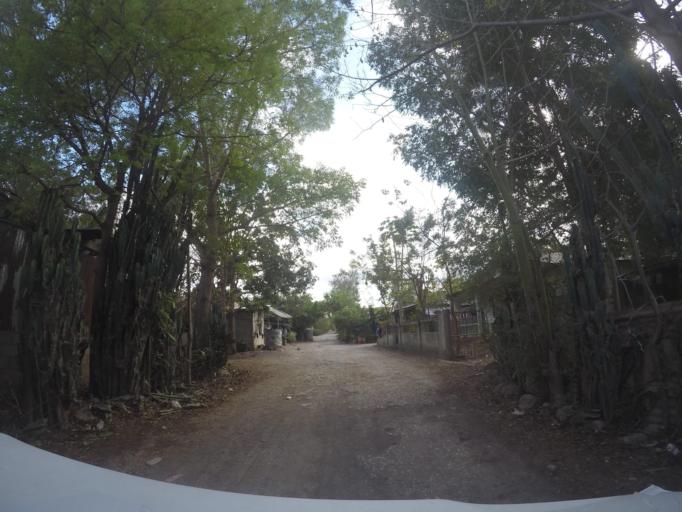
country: TL
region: Baucau
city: Baucau
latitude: -8.4768
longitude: 126.4571
